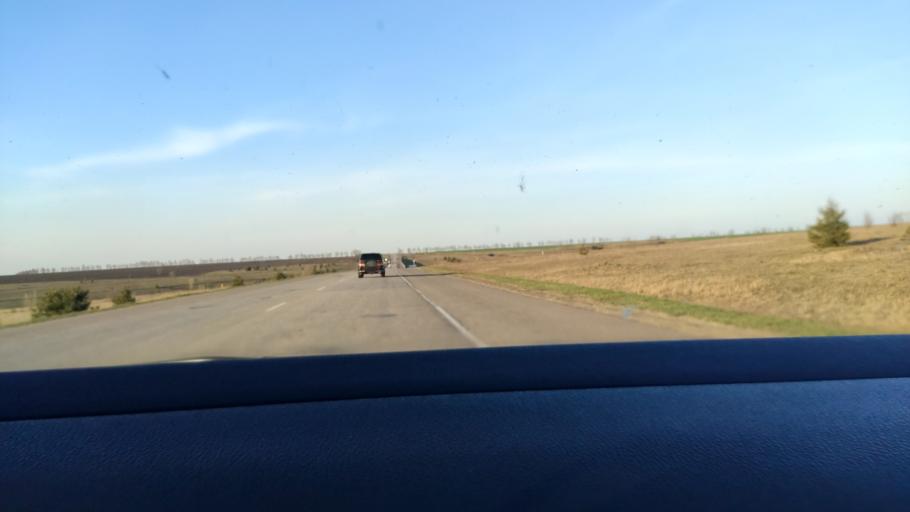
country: RU
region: Voronezj
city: Kolodeznyy
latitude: 51.3832
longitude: 39.2200
